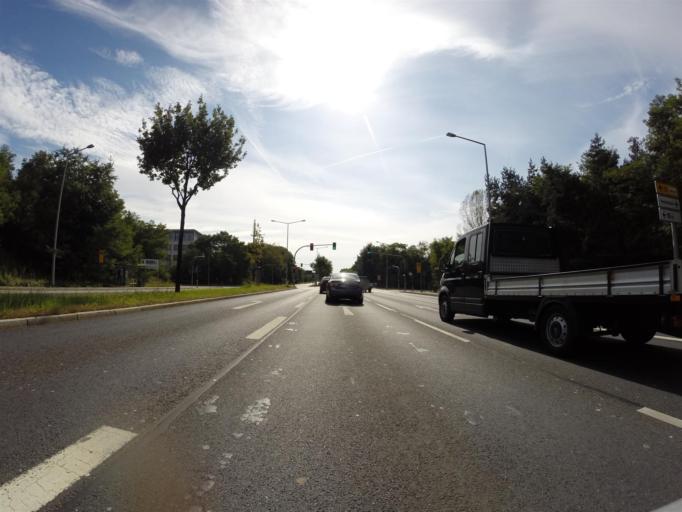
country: DE
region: Saxony
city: Albertstadt
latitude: 51.1003
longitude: 13.7357
